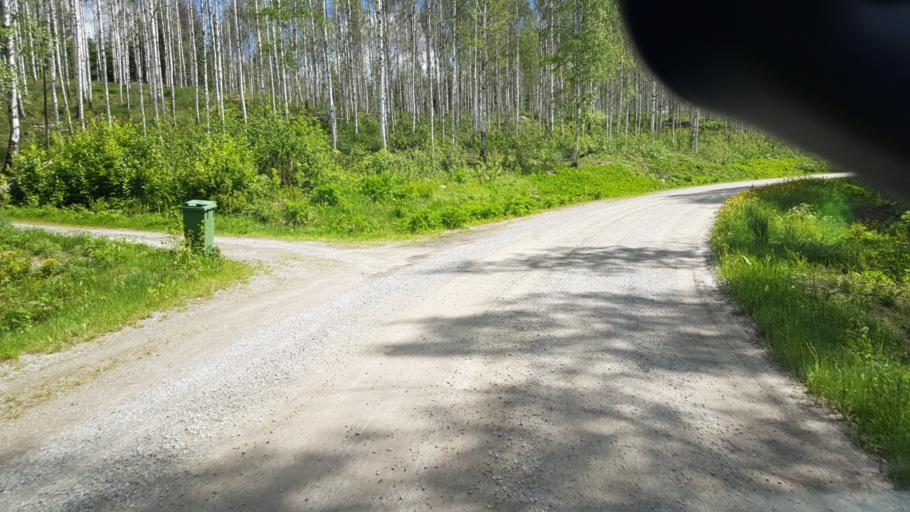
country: SE
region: Vaermland
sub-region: Arvika Kommun
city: Arvika
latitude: 59.7158
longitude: 12.8454
